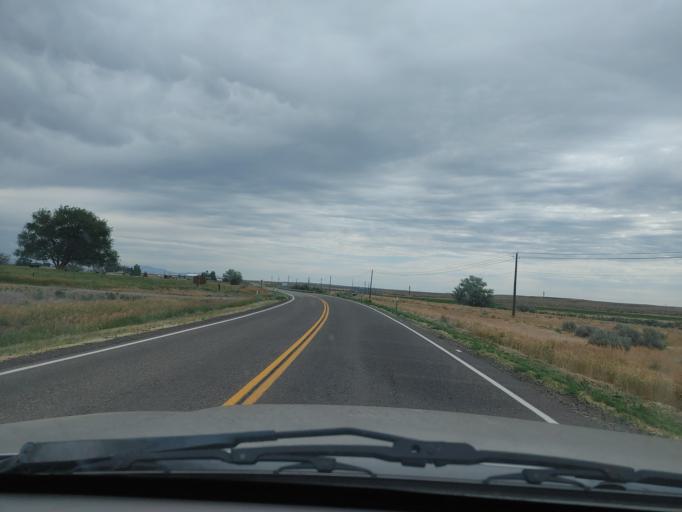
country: US
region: Idaho
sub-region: Lincoln County
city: Shoshone
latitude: 43.0501
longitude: -114.1424
